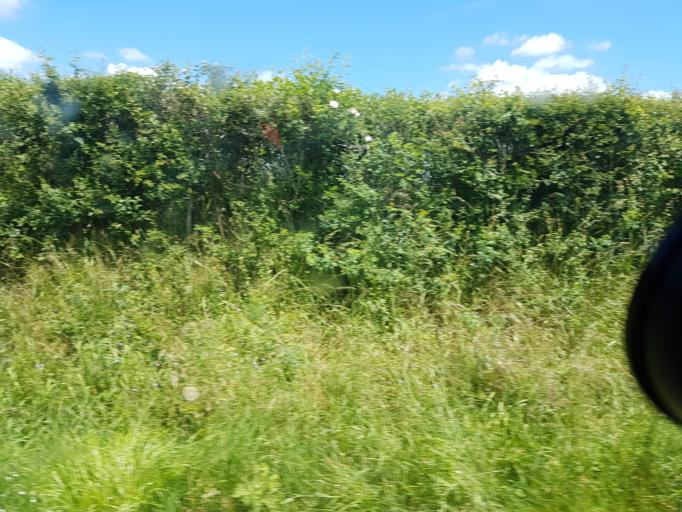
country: FR
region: Bourgogne
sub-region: Departement de Saone-et-Loire
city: Curgy
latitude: 47.0370
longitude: 4.4068
